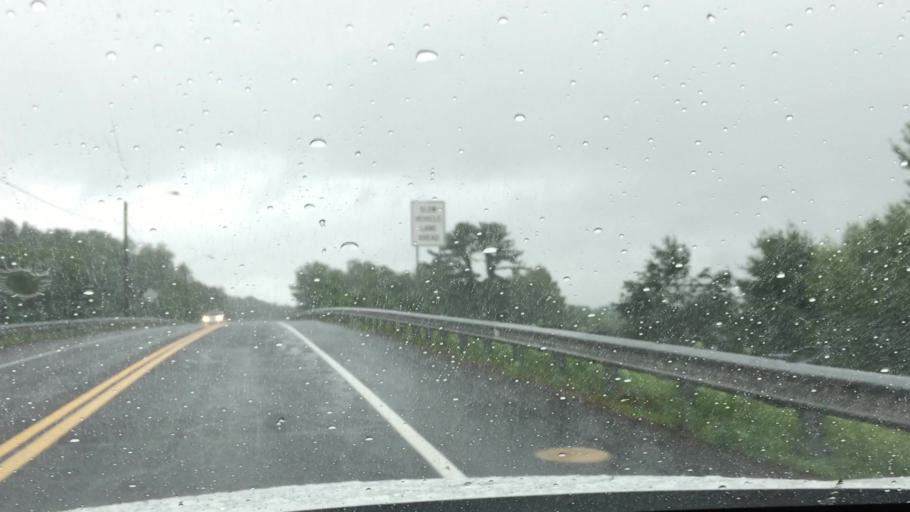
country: US
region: Massachusetts
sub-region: Berkshire County
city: Lanesborough
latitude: 42.4908
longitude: -73.2124
